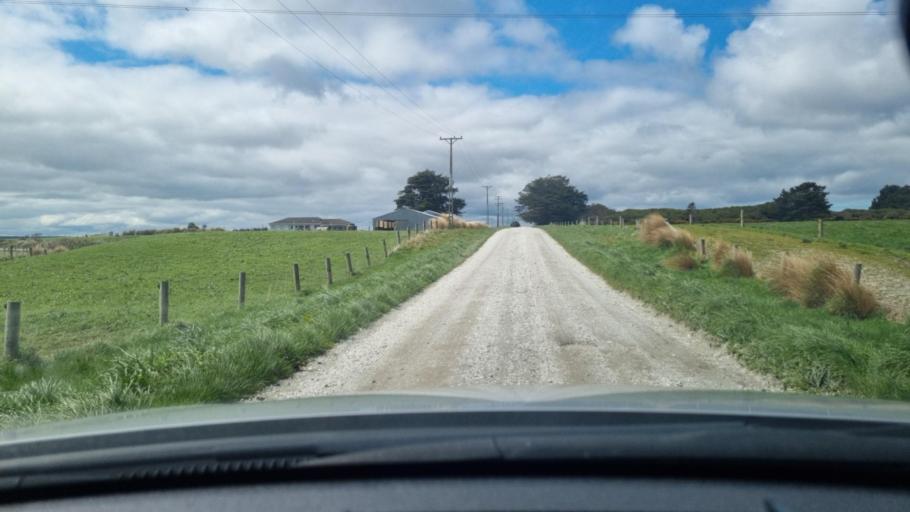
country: NZ
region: Southland
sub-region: Invercargill City
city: Invercargill
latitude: -46.5067
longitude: 168.4352
